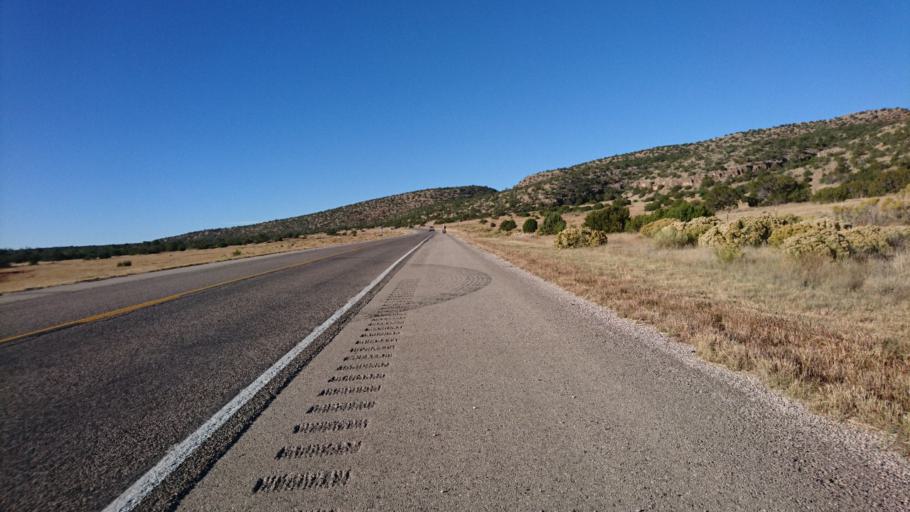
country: US
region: New Mexico
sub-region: Cibola County
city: Grants
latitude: 34.9791
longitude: -107.9075
